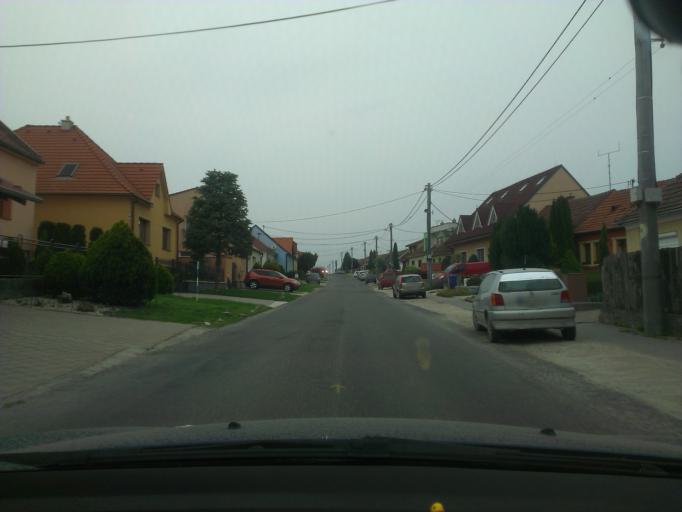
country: SK
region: Trnavsky
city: Vrbove
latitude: 48.5921
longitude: 17.7535
